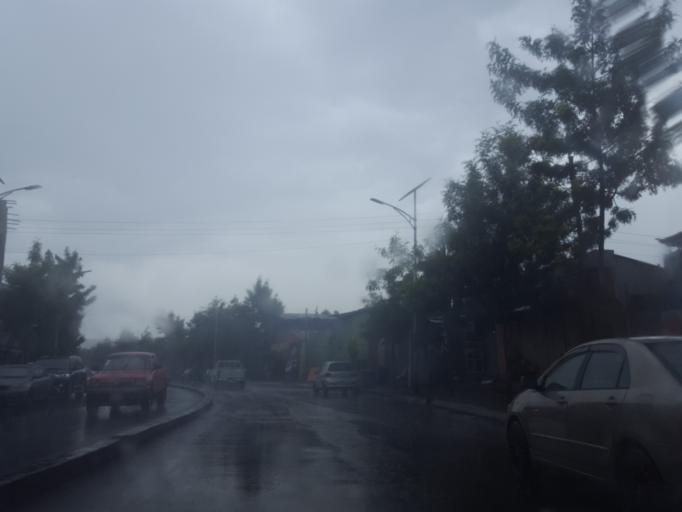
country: ET
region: Adis Abeba
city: Addis Ababa
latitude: 9.0190
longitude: 38.7824
